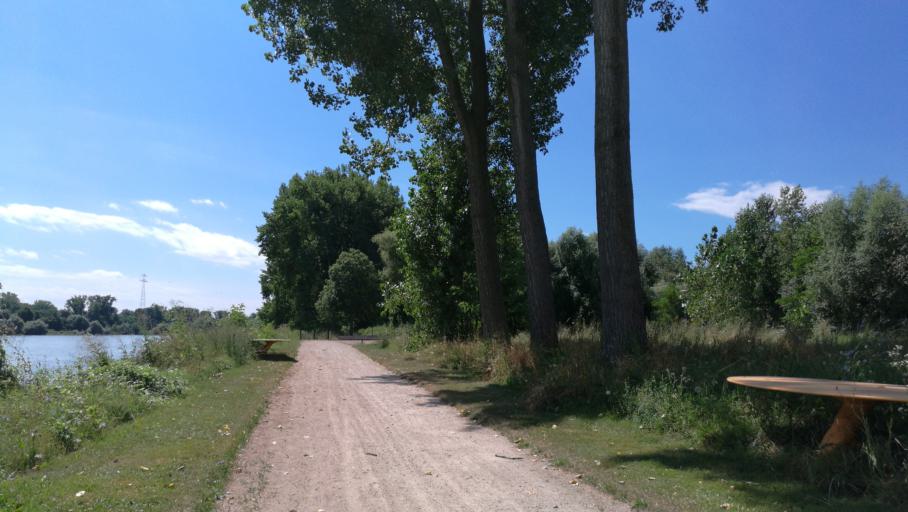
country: DE
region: Baden-Wuerttemberg
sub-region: Freiburg Region
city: Kehl
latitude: 48.5644
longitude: 7.8031
